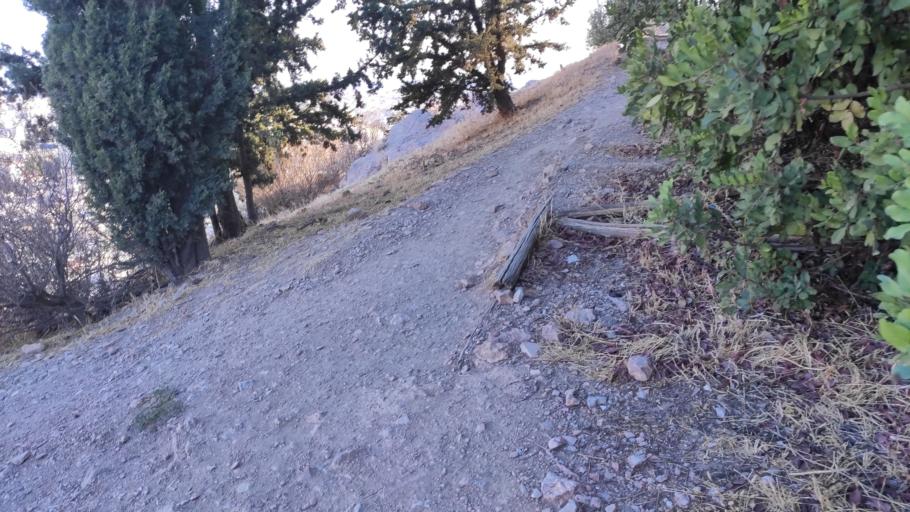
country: GR
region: Attica
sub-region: Nomarchia Athinas
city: Athens
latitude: 37.9671
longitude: 23.7218
